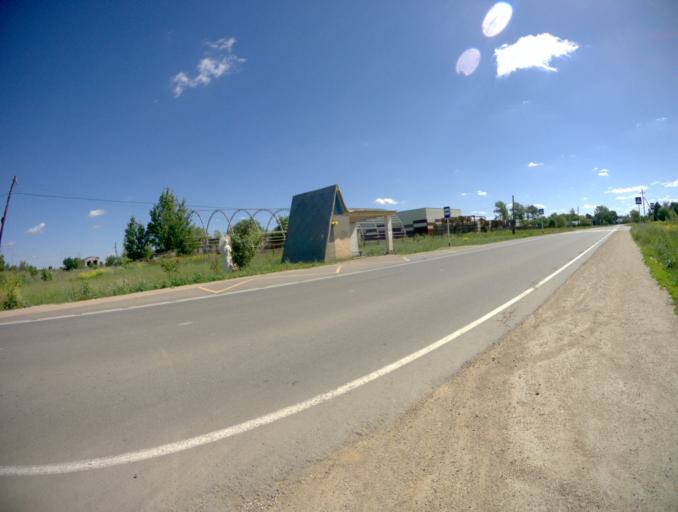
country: RU
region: Ivanovo
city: Petrovskiy
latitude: 56.5177
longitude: 40.2588
